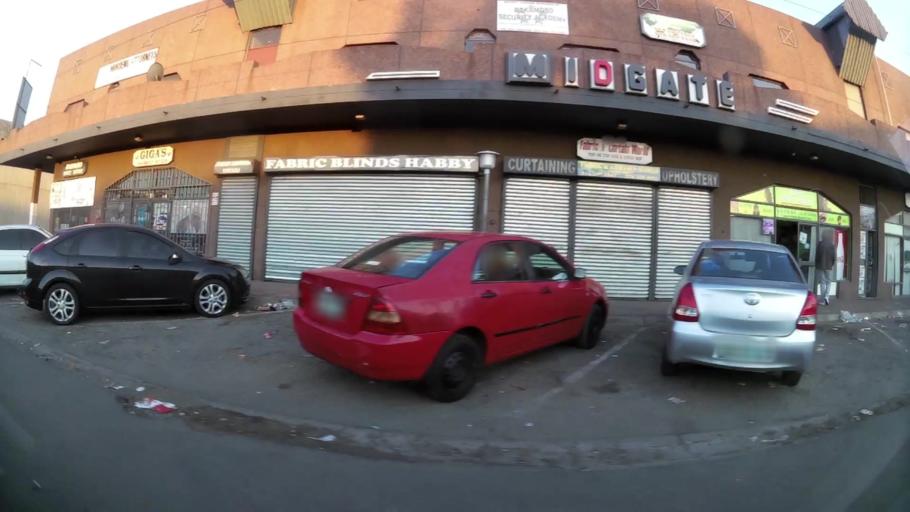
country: ZA
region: North-West
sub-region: Bojanala Platinum District Municipality
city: Rustenburg
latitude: -25.6692
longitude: 27.2410
